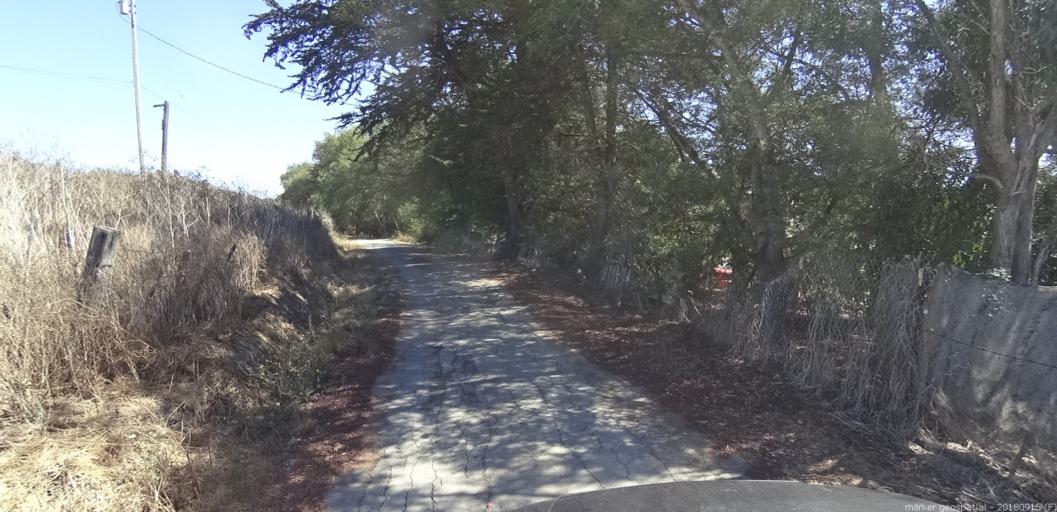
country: US
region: California
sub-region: Monterey County
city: Las Lomas
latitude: 36.8600
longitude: -121.7563
